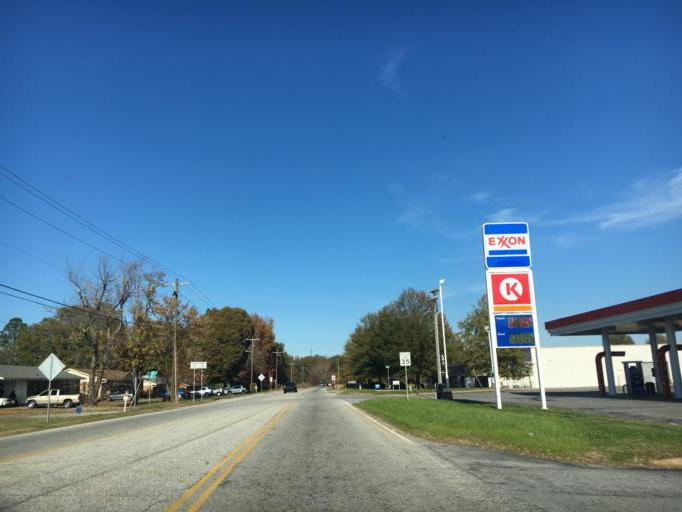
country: US
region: South Carolina
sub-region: Spartanburg County
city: Southern Shops
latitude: 35.0102
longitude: -82.0276
